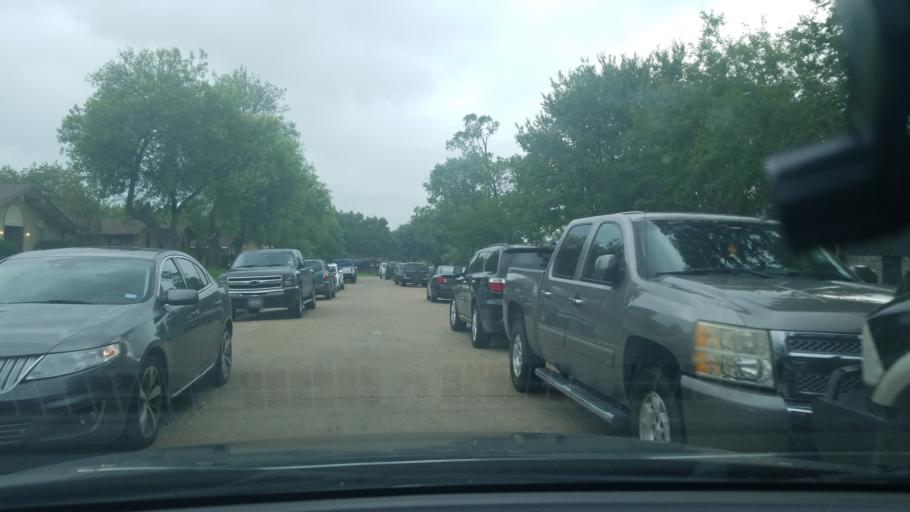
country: US
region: Texas
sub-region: Dallas County
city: Mesquite
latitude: 32.7821
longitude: -96.6371
